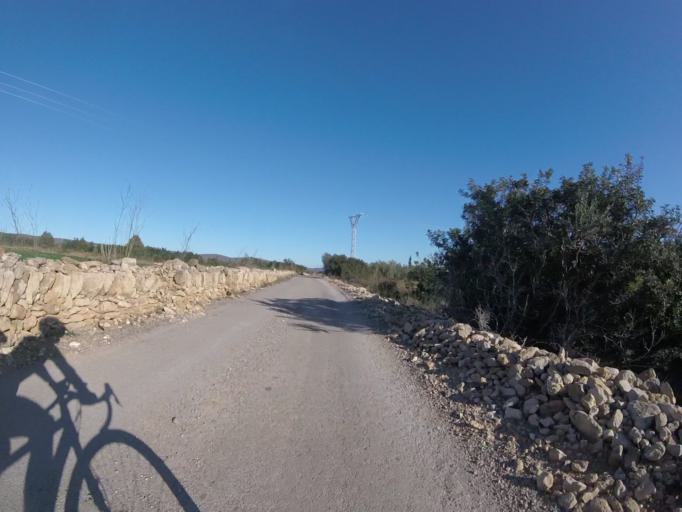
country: ES
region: Valencia
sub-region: Provincia de Castello
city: Alcala de Xivert
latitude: 40.2831
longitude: 0.2115
